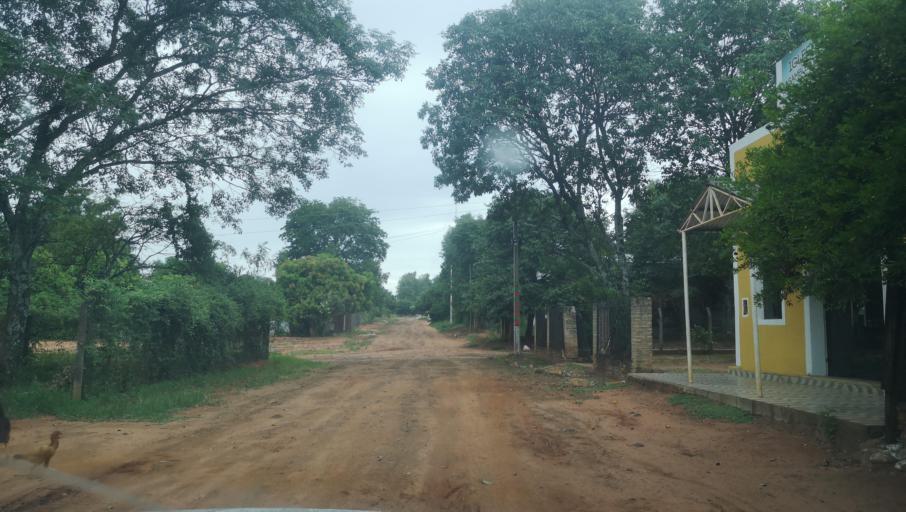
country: PY
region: San Pedro
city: Capiibary
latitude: -24.7269
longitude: -56.0144
